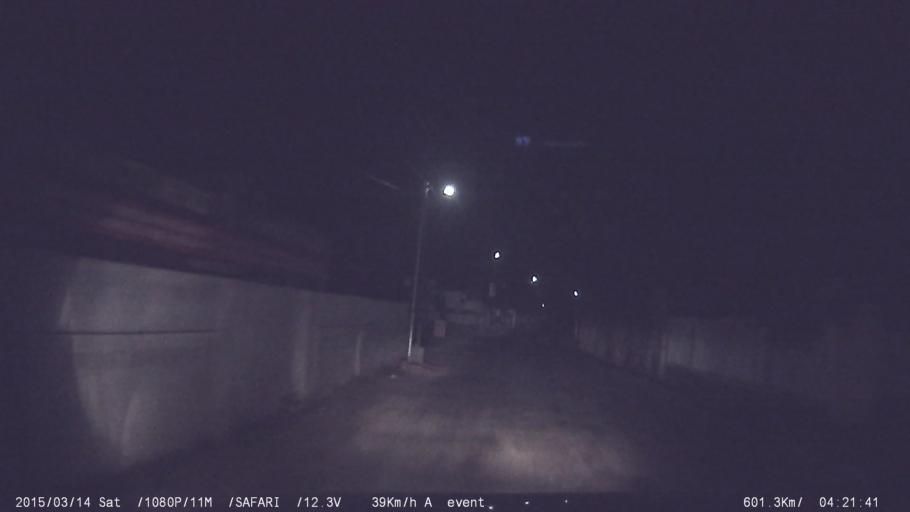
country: IN
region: Kerala
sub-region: Kottayam
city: Changanacheri
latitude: 9.4445
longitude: 76.5477
